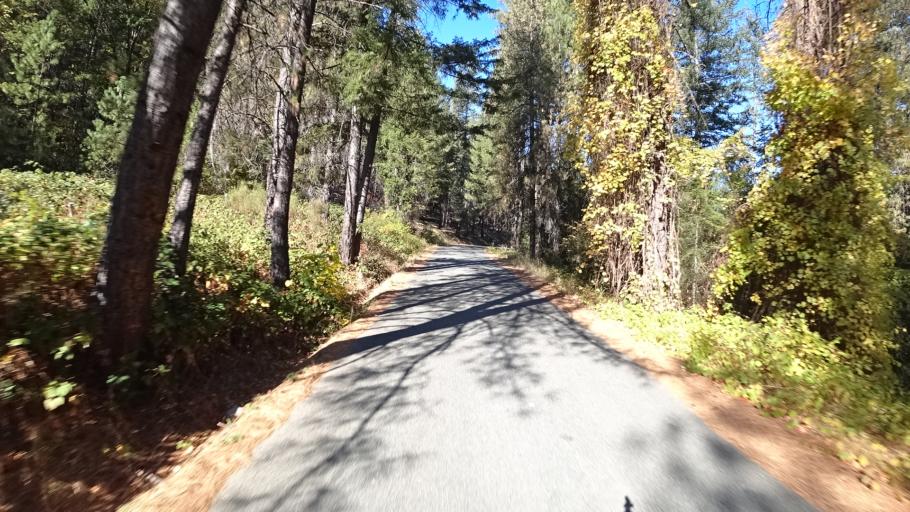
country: US
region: California
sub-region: Siskiyou County
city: Happy Camp
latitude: 41.7554
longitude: -123.0128
